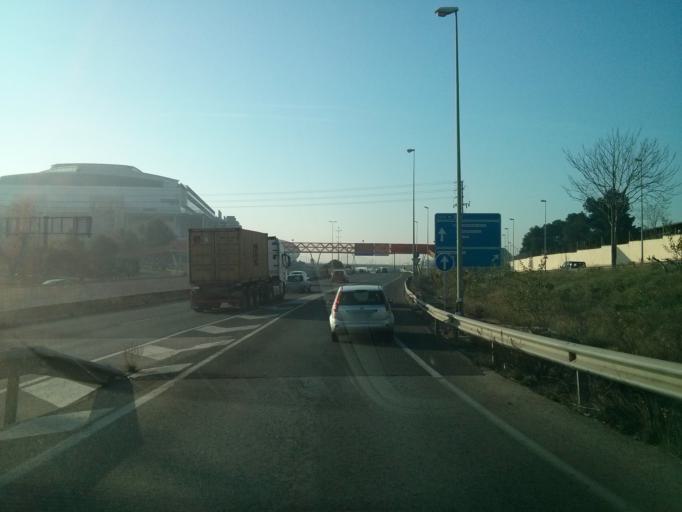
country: ES
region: Valencia
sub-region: Provincia de Valencia
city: Paterna
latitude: 39.5075
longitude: -0.4332
